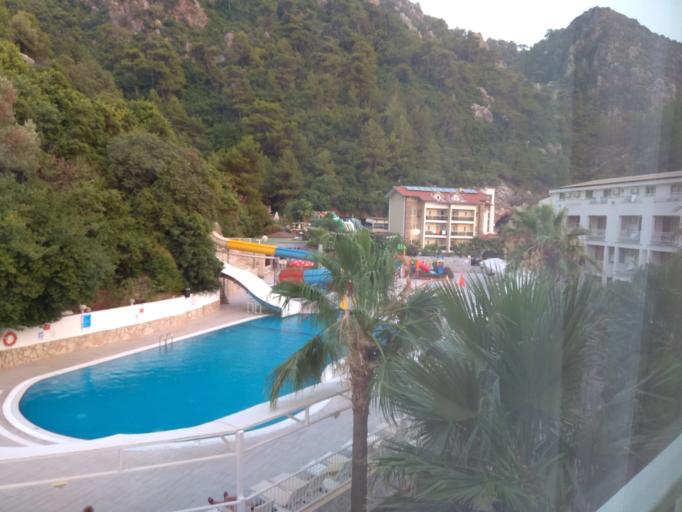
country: TR
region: Mugla
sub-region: Marmaris
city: Marmaris
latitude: 36.7980
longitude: 28.2349
